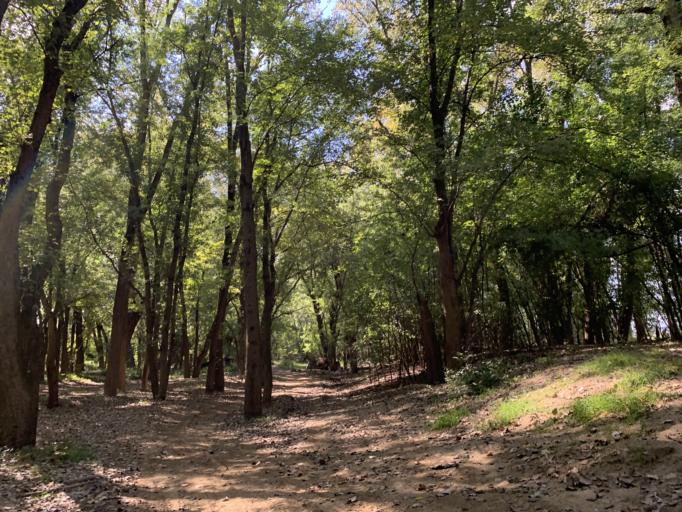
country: US
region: Indiana
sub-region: Floyd County
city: New Albany
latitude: 38.2794
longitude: -85.8092
